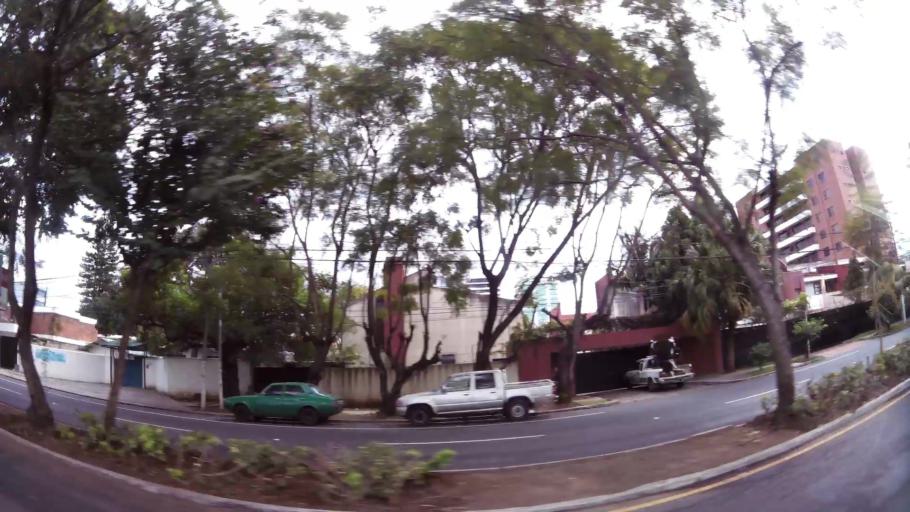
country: GT
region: Guatemala
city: Santa Catarina Pinula
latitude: 14.5831
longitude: -90.5234
